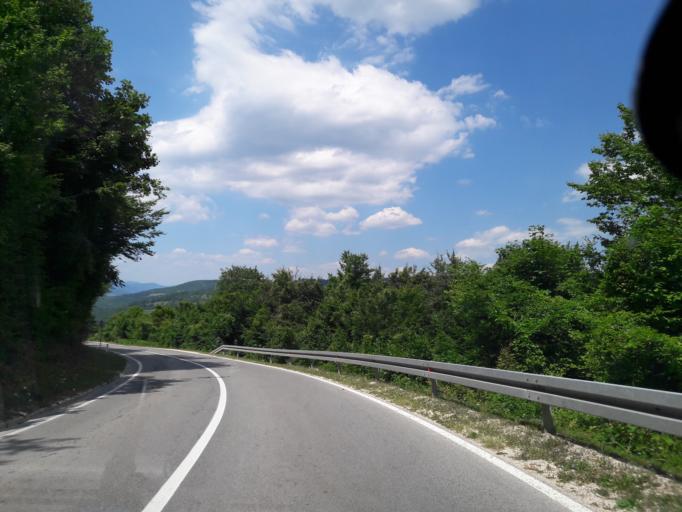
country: BA
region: Republika Srpska
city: Sipovo
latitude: 44.1975
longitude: 17.1530
